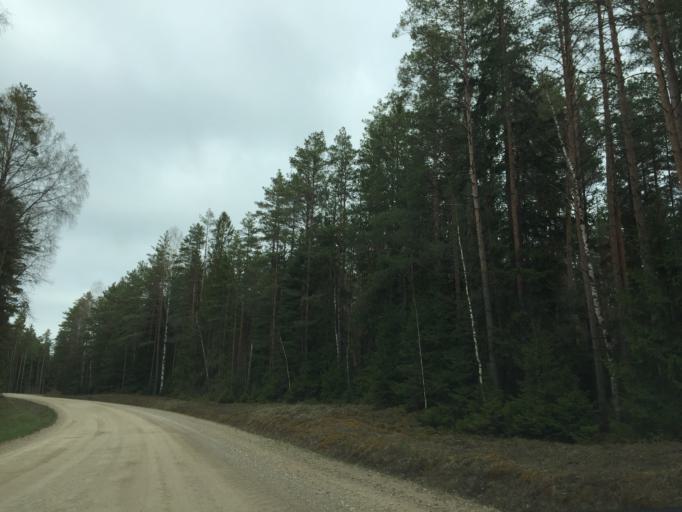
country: EE
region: Valgamaa
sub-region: Valga linn
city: Valga
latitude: 57.5917
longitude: 26.2207
